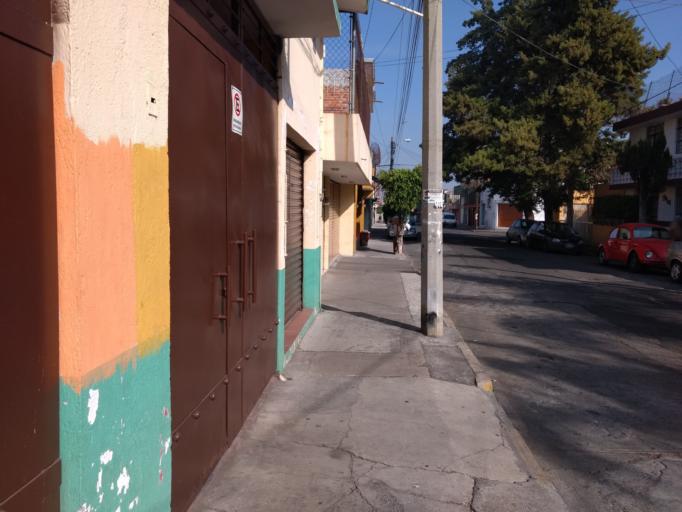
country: MX
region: Michoacan
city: Morelia
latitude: 19.7048
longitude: -101.2099
